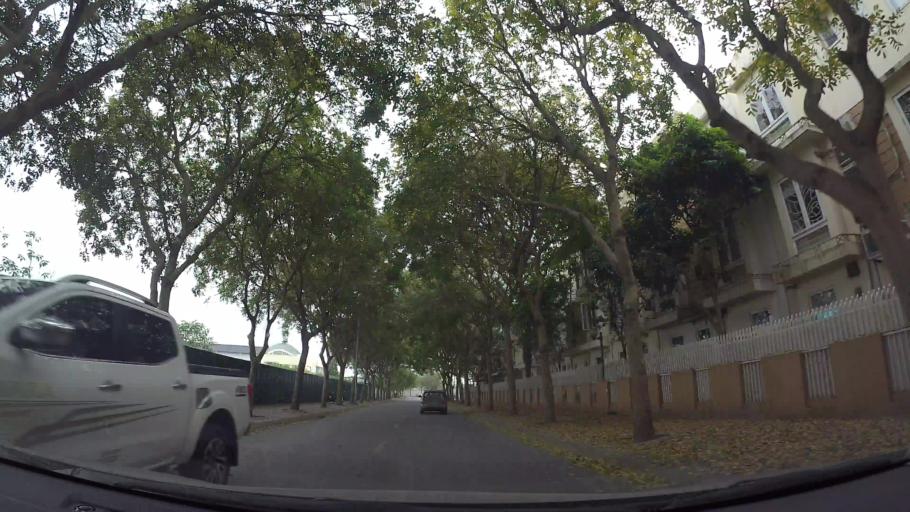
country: VN
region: Ha Noi
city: Trau Quy
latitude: 21.0566
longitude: 105.9062
